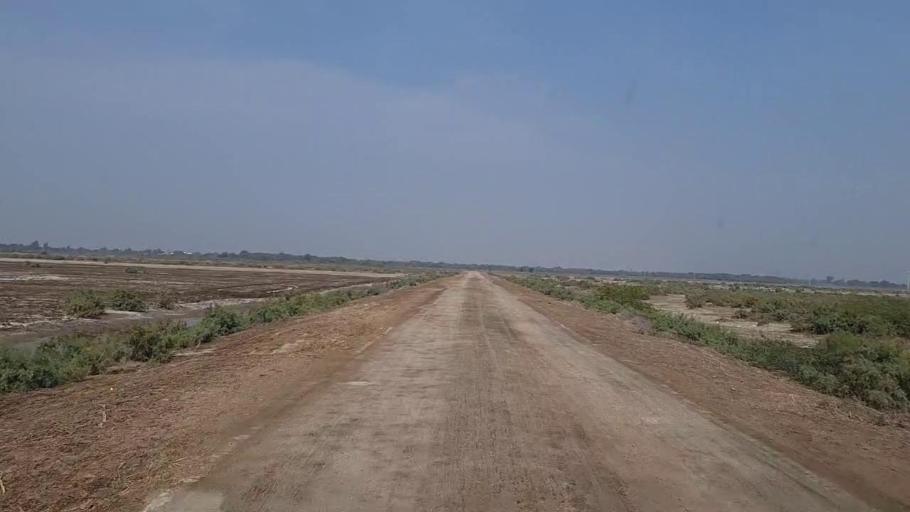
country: PK
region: Sindh
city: Mirwah Gorchani
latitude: 25.3306
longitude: 69.0615
